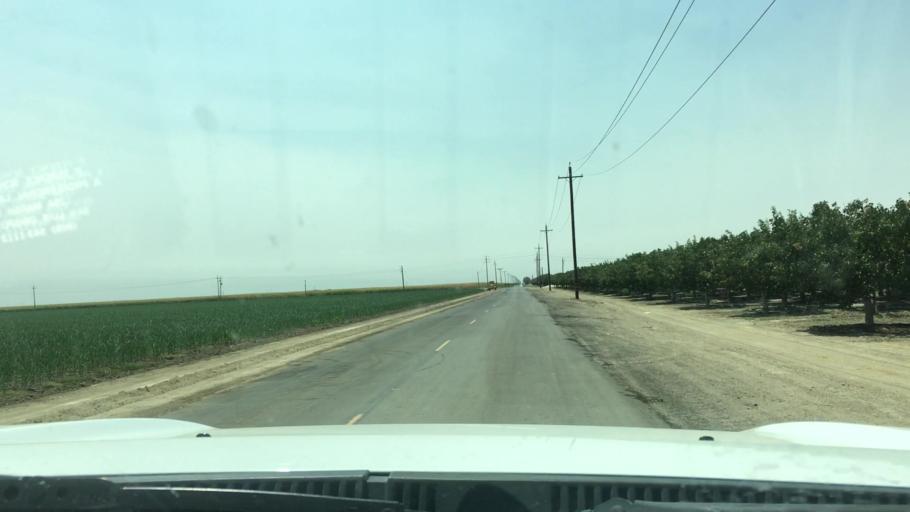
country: US
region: California
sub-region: Kern County
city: Wasco
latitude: 35.7207
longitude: -119.4372
